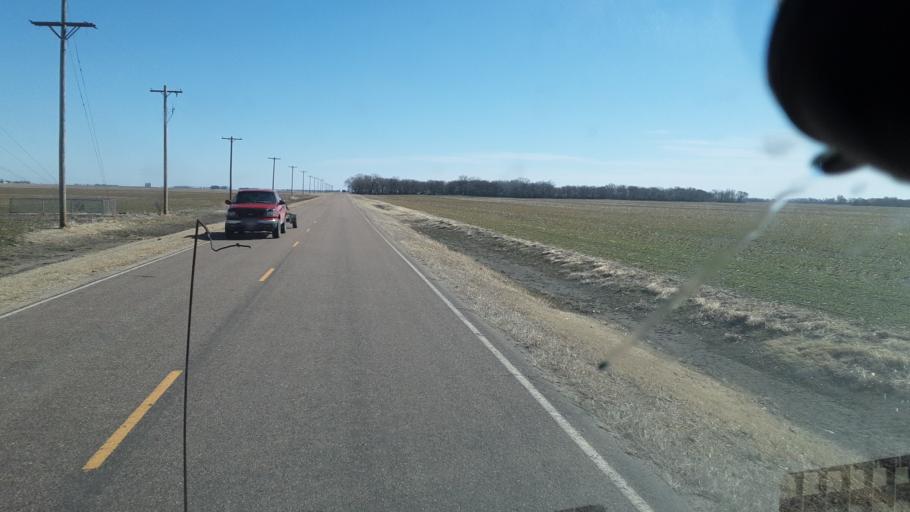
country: US
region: Kansas
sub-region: Rice County
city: Sterling
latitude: 38.2462
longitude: -98.3021
